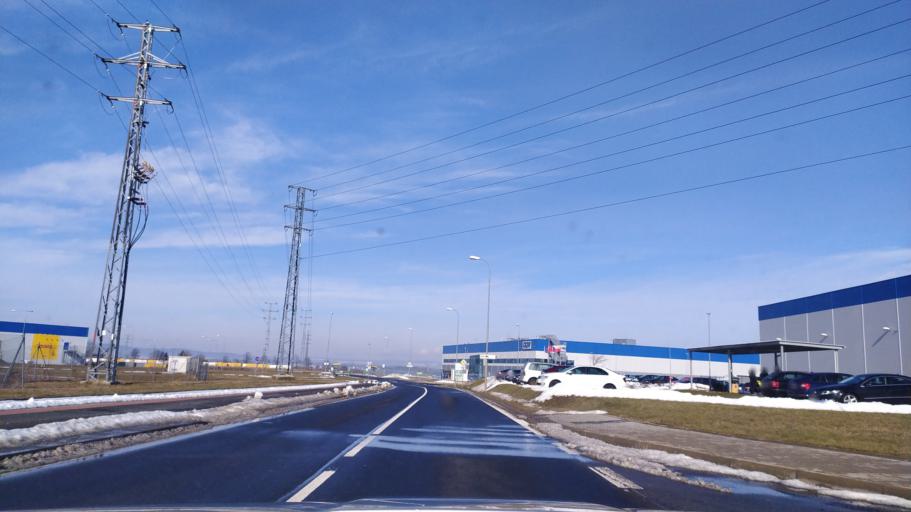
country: CZ
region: Karlovarsky
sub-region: Okres Cheb
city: Cheb
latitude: 50.0893
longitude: 12.4071
